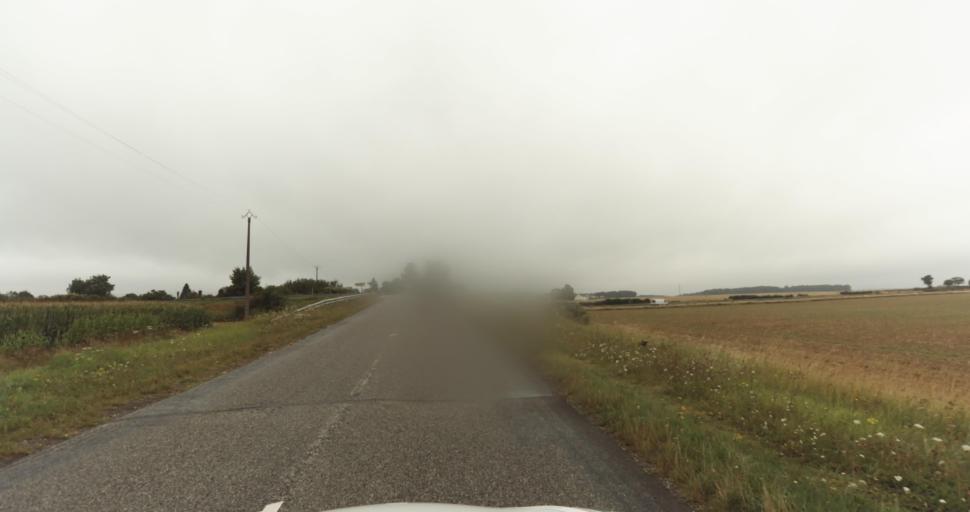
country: FR
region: Haute-Normandie
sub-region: Departement de l'Eure
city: Normanville
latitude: 49.0807
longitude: 1.1900
